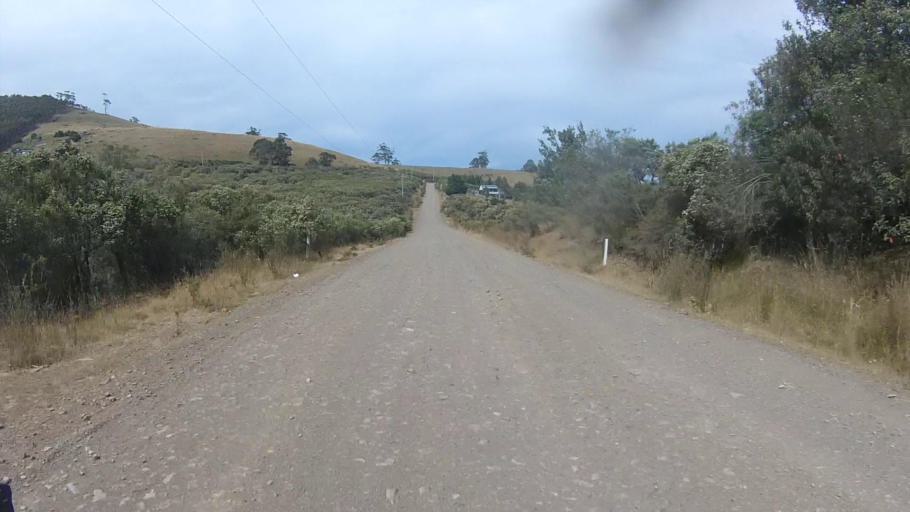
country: AU
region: Tasmania
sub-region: Sorell
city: Sorell
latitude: -42.7744
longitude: 147.8296
